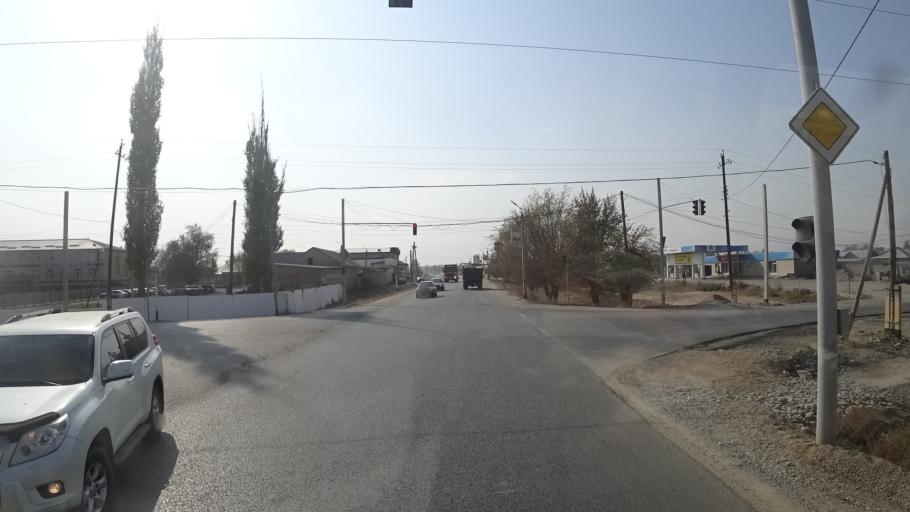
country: KZ
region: Zhambyl
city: Sarykemer
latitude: 43.0095
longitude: 71.5103
